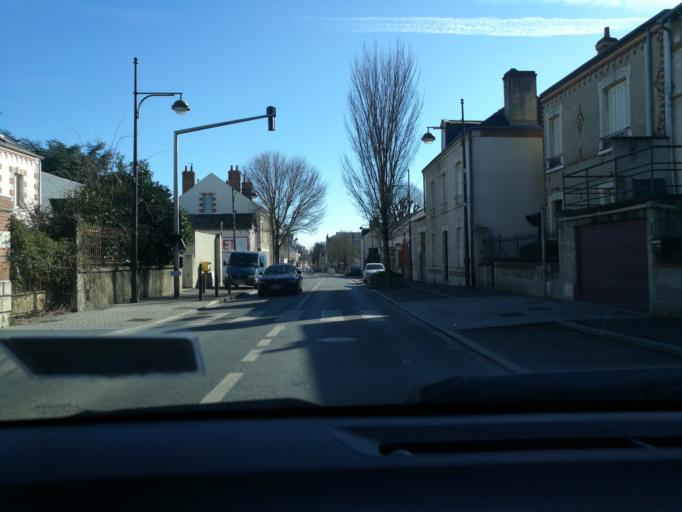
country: FR
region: Centre
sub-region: Departement du Loiret
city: Orleans
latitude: 47.9074
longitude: 1.8875
